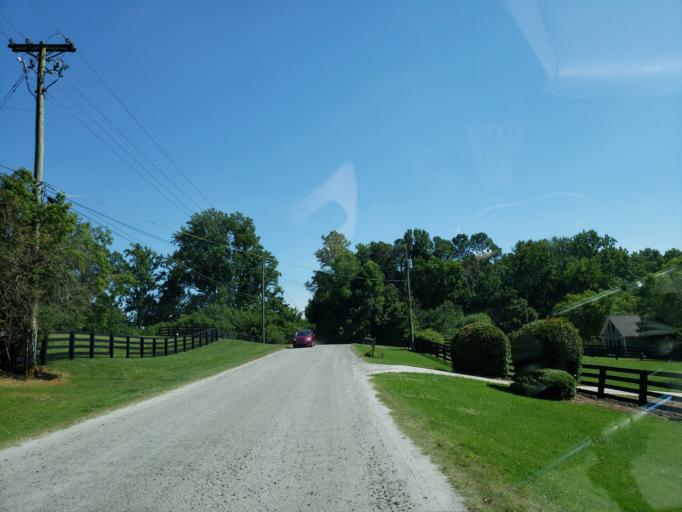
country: US
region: Georgia
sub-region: Fulton County
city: Milton
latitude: 34.1188
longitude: -84.3109
